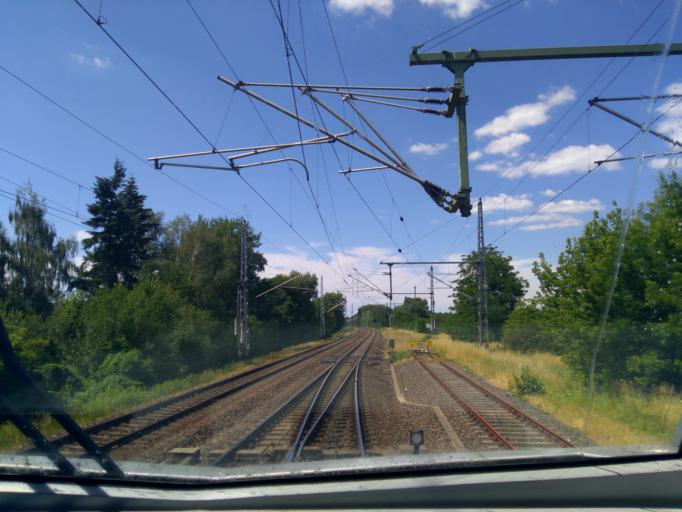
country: DE
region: Brandenburg
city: Bad Wilsnack
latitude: 52.9615
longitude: 11.9465
